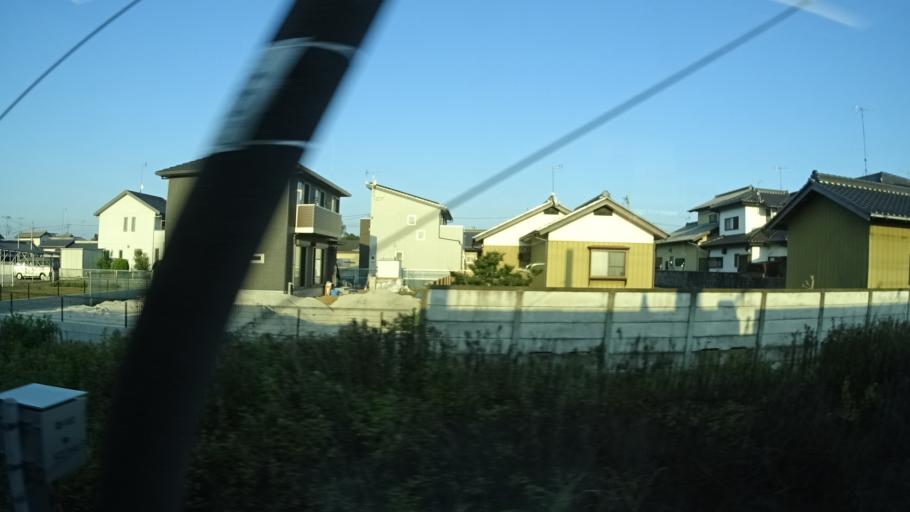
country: JP
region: Ibaraki
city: Ishioka
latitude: 36.2084
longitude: 140.2809
